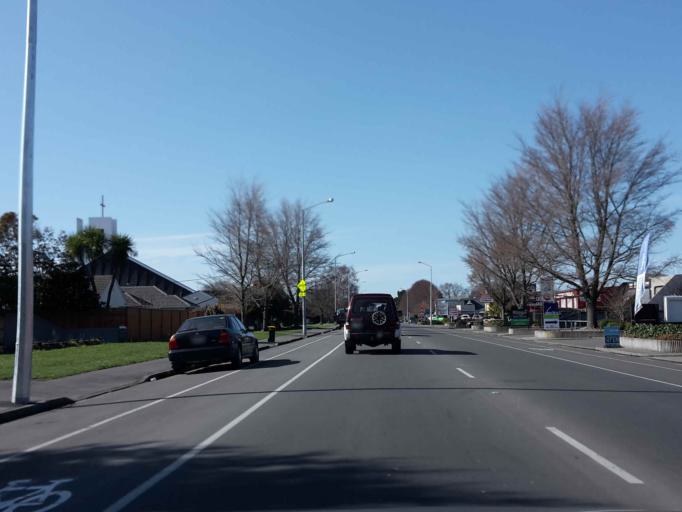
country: NZ
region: Canterbury
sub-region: Selwyn District
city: Prebbleton
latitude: -43.5370
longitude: 172.5580
